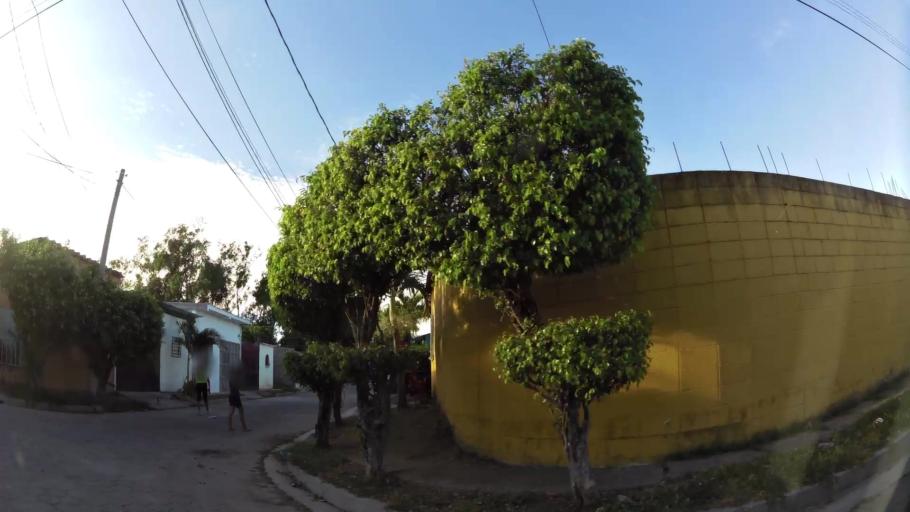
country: SV
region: Santa Ana
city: Metapan
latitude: 14.3325
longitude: -89.4528
